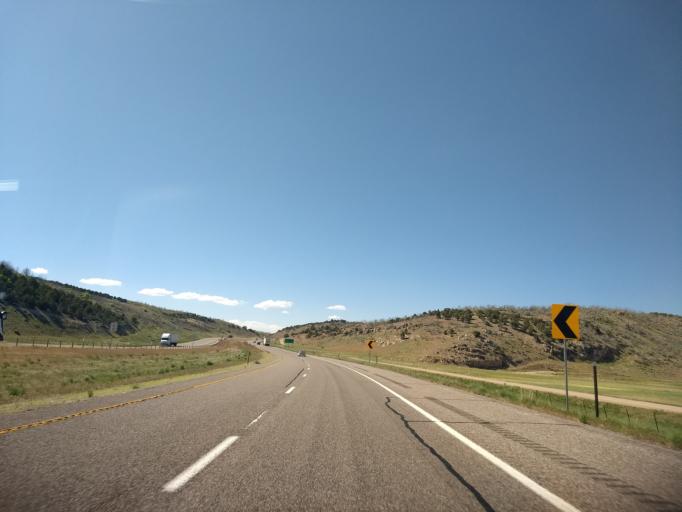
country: US
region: Utah
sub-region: Millard County
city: Fillmore
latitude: 38.6729
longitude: -112.5893
